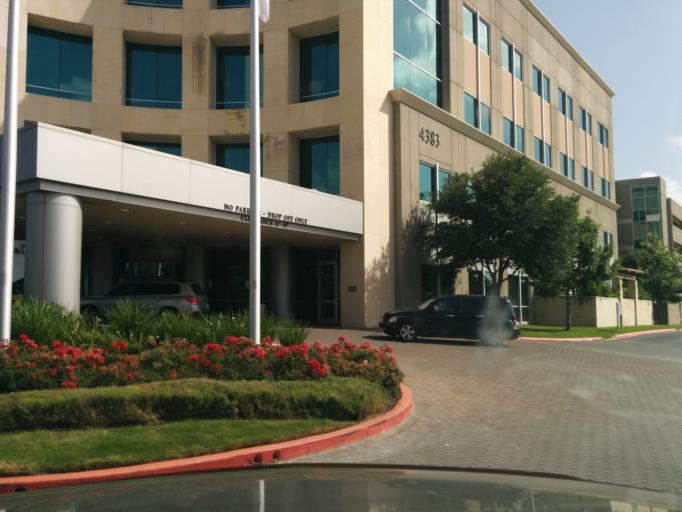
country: US
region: Texas
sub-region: Bexar County
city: Balcones Heights
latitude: 29.5113
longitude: -98.5720
